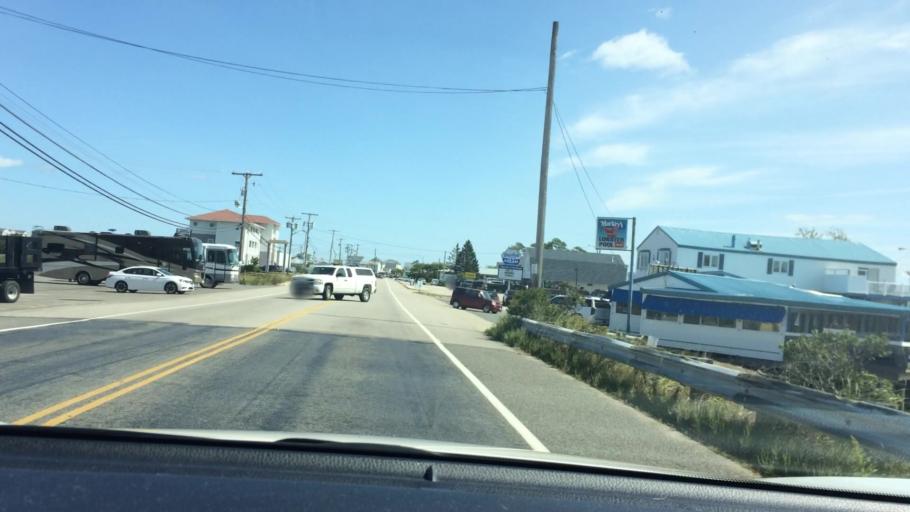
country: US
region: New Hampshire
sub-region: Rockingham County
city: Hampton Beach
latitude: 42.8714
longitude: -70.8234
